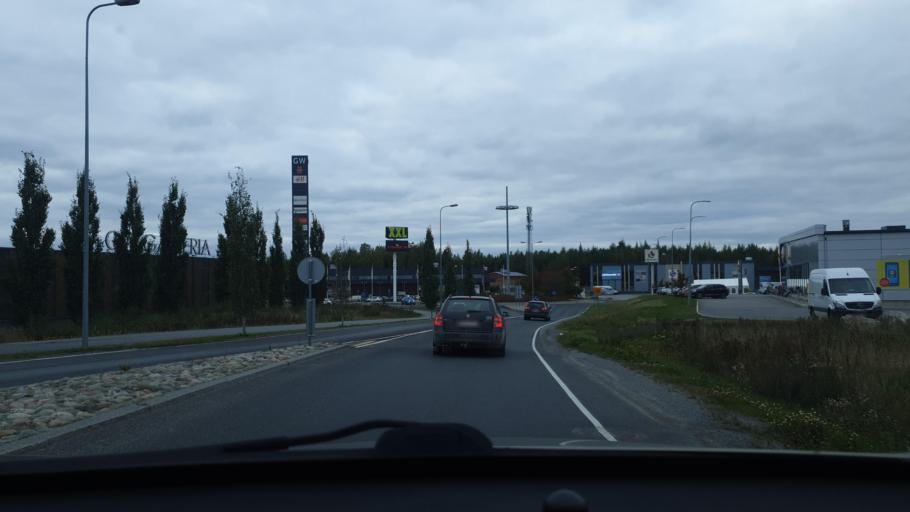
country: FI
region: Ostrobothnia
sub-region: Vaasa
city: Korsholm
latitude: 63.1123
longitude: 21.6592
